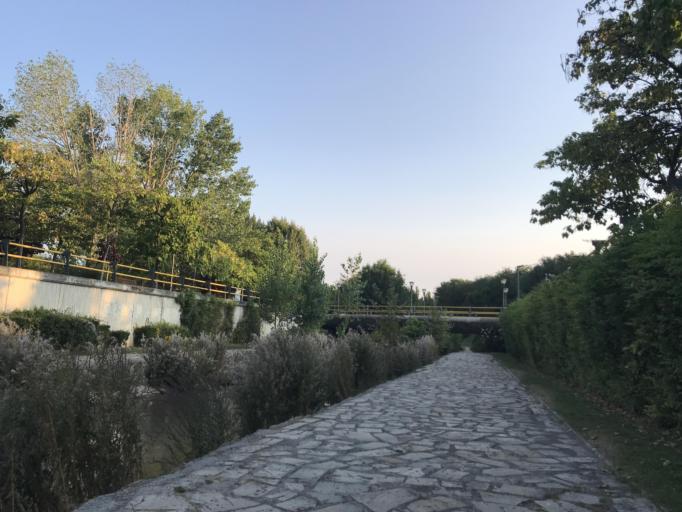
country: ES
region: Castille and Leon
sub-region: Provincia de Valladolid
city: Valladolid
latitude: 41.6561
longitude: -4.7112
